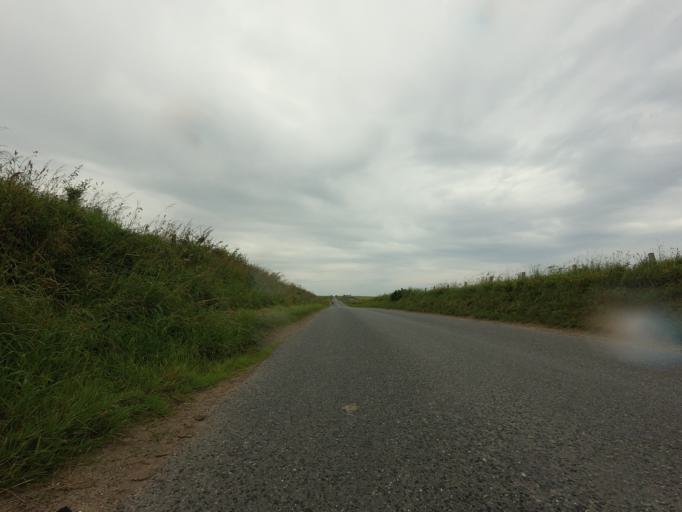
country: GB
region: Scotland
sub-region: Aberdeenshire
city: Whitehills
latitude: 57.6707
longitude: -2.6164
